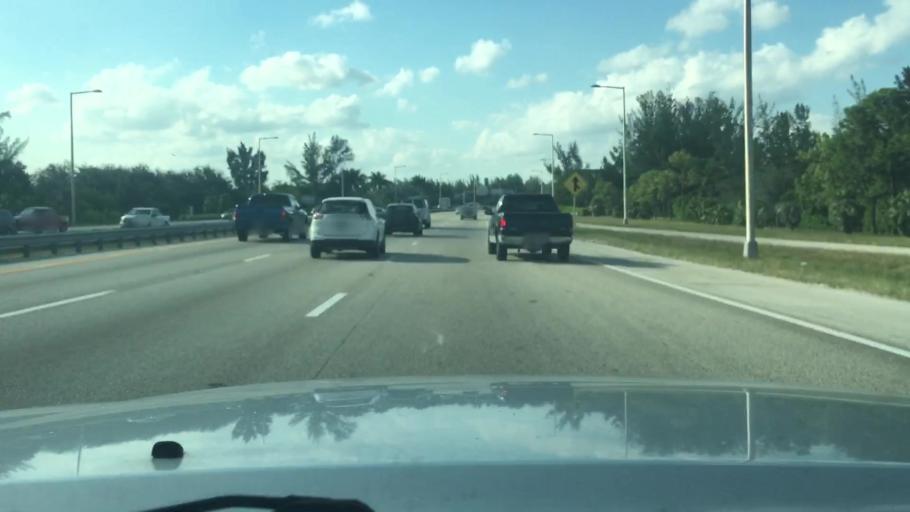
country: US
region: Florida
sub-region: Miami-Dade County
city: Opa-locka
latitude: 25.8876
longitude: -80.2724
